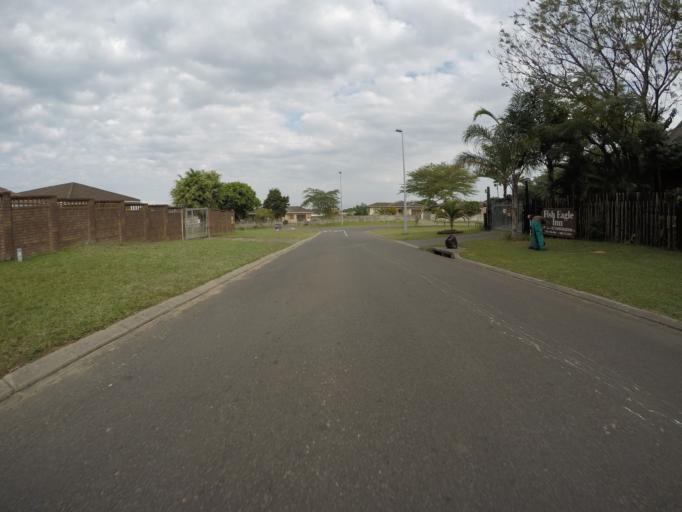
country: ZA
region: KwaZulu-Natal
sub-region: uThungulu District Municipality
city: Richards Bay
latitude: -28.7363
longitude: 32.0898
